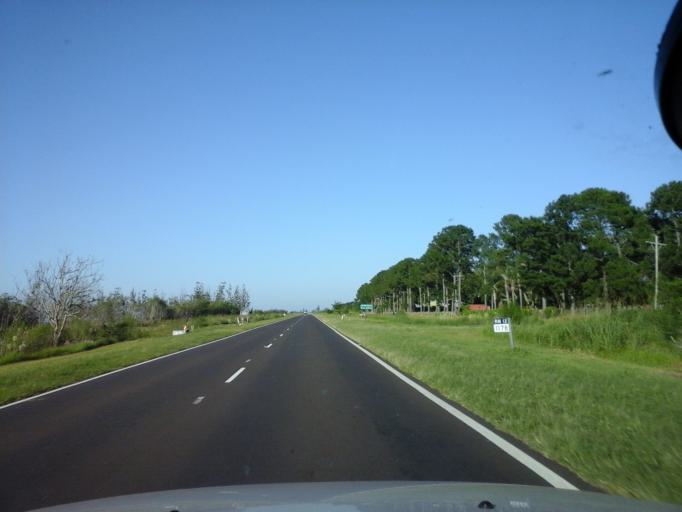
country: AR
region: Corrientes
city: Ita Ibate
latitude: -27.4475
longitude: -57.3971
